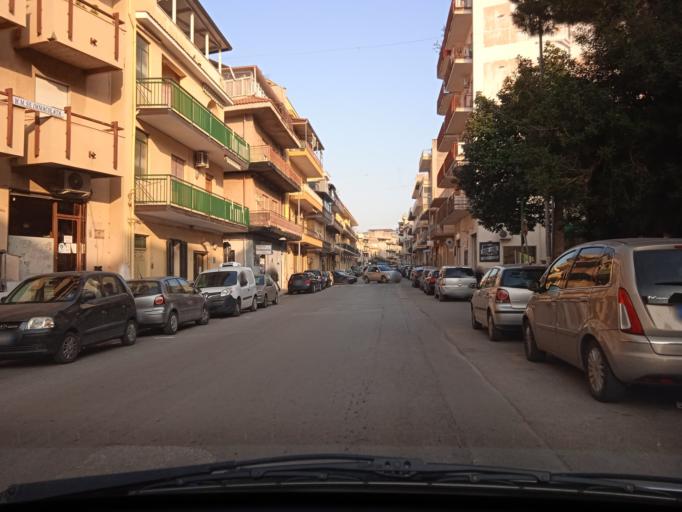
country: IT
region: Sicily
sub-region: Palermo
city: Villabate
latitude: 38.0754
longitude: 13.4471
